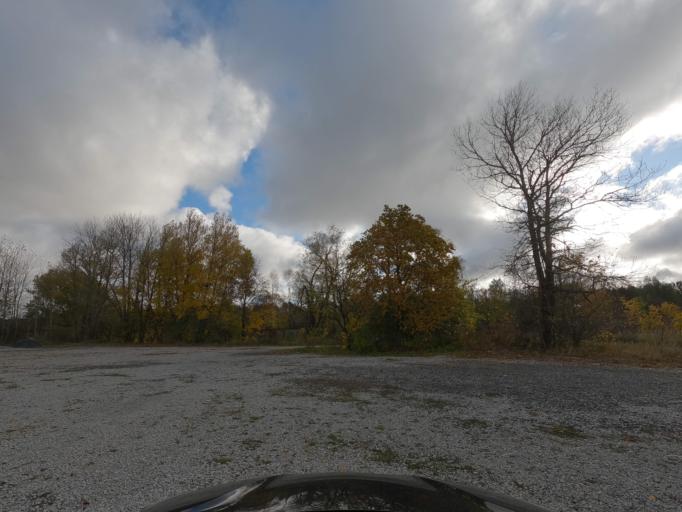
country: EE
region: Harju
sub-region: Tallinna linn
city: Tallinn
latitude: 59.4073
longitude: 24.7386
